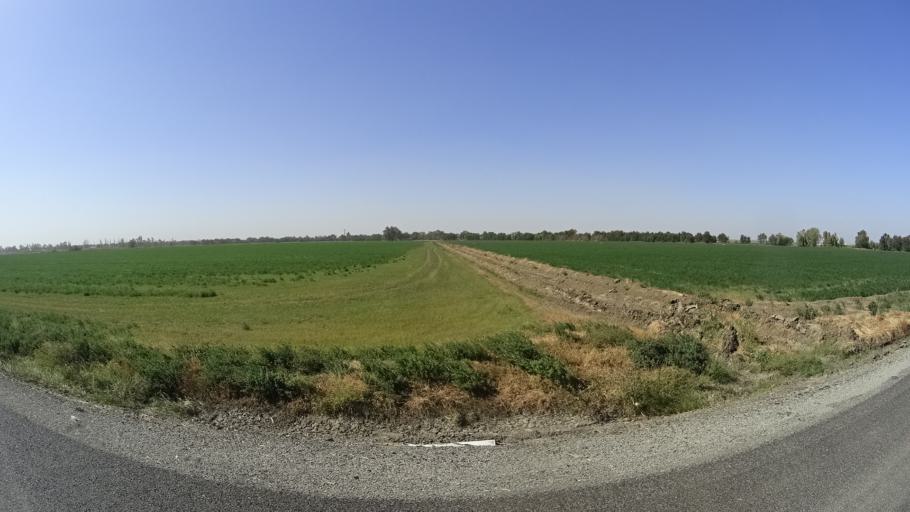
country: US
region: California
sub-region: Yolo County
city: Woodland
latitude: 38.6235
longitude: -121.7295
